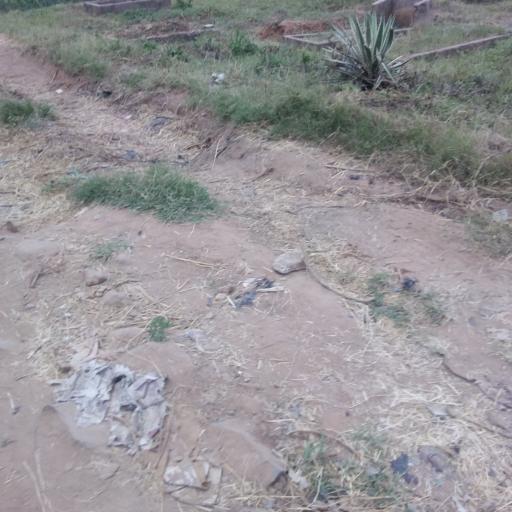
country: TZ
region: Mwanza
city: Mwanza
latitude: -2.4811
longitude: 32.9035
